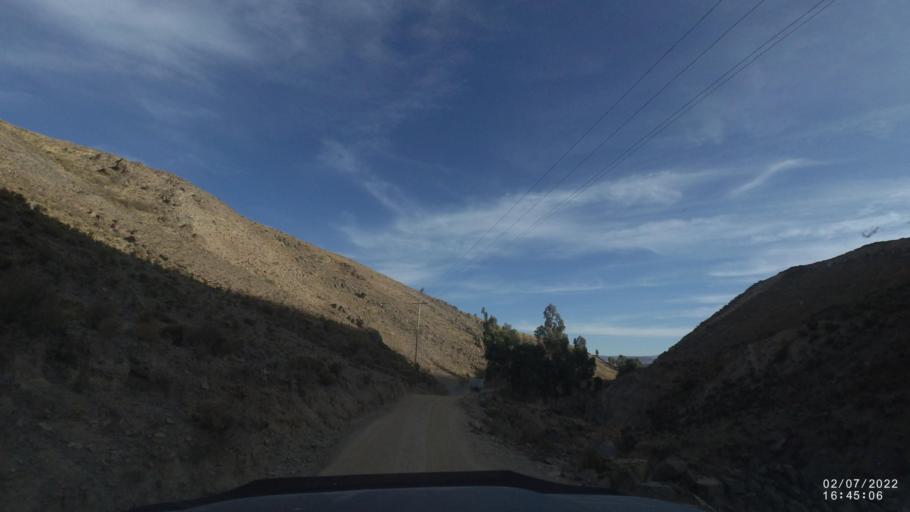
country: BO
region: Cochabamba
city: Irpa Irpa
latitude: -17.9748
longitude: -66.5098
